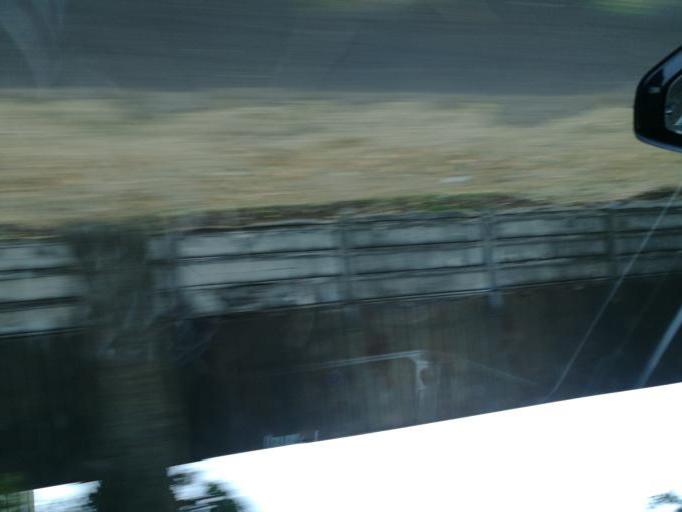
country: RO
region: Galati
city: Galati
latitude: 45.4601
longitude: 28.0280
